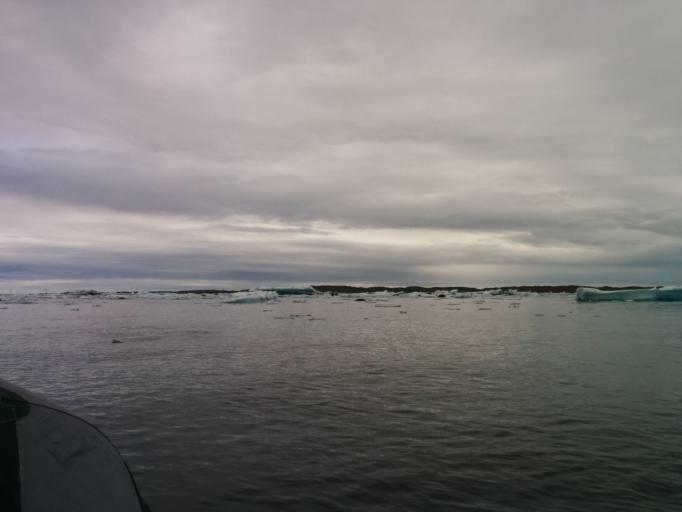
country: IS
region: East
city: Hoefn
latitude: 64.0610
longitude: -16.2099
